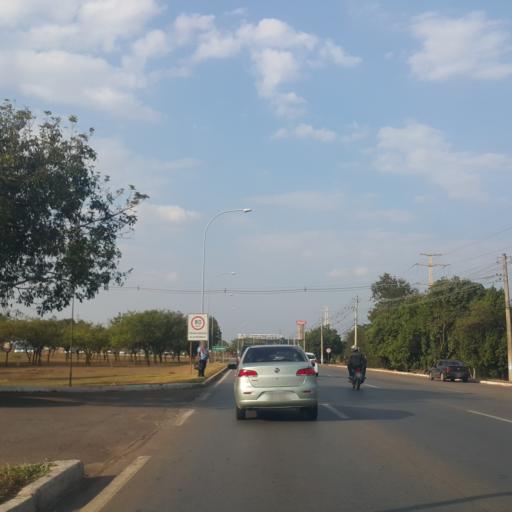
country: BR
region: Federal District
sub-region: Brasilia
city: Brasilia
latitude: -15.8763
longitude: -48.0483
